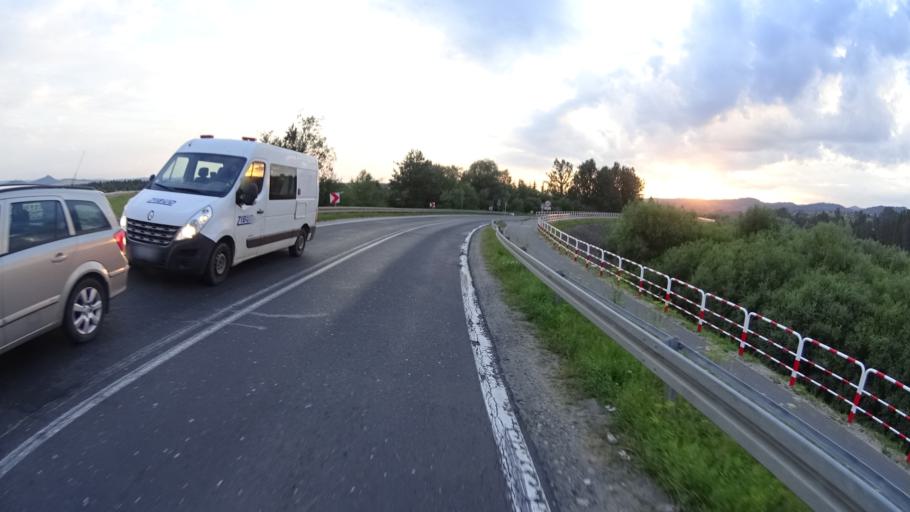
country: PL
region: Lesser Poland Voivodeship
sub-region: Powiat nowotarski
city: Frydman
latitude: 49.4667
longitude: 20.2209
